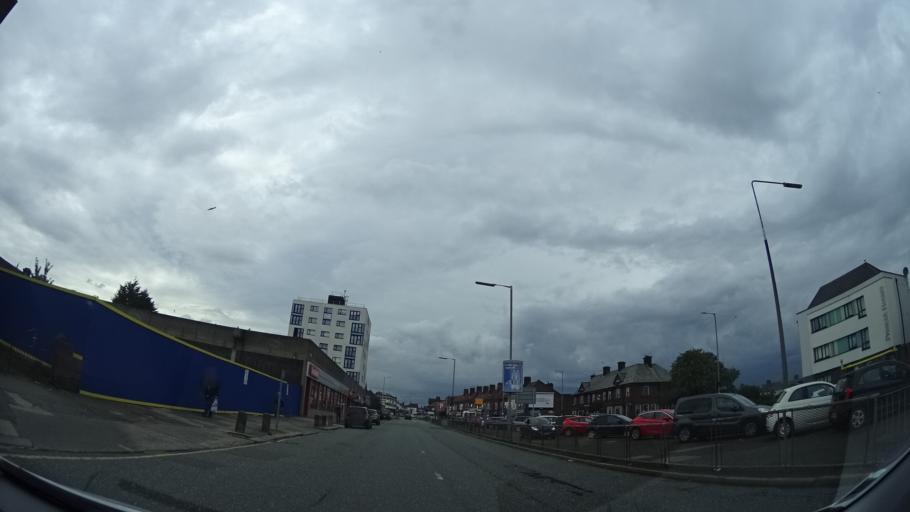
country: GB
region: England
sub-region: Knowsley
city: Knowsley
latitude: 53.4150
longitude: -2.9066
